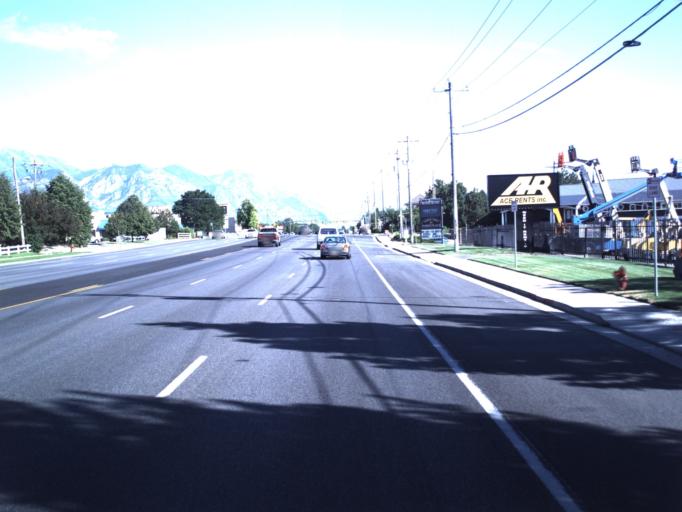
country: US
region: Utah
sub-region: Utah County
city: Lindon
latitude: 40.3369
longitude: -111.7162
